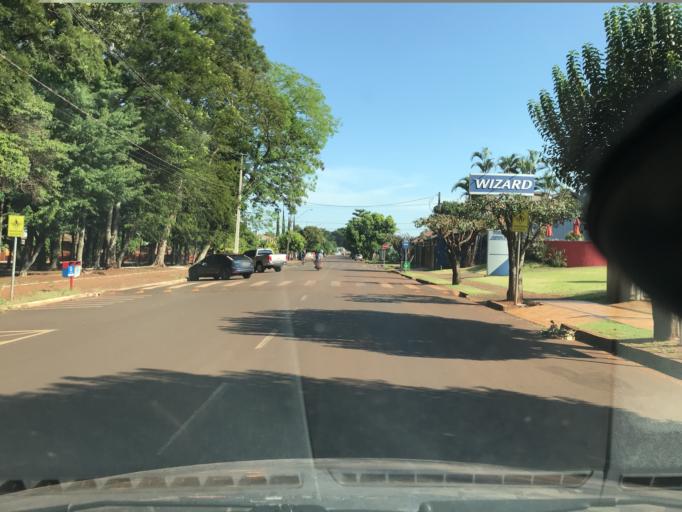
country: BR
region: Parana
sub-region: Palotina
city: Palotina
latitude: -24.2825
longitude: -53.8427
